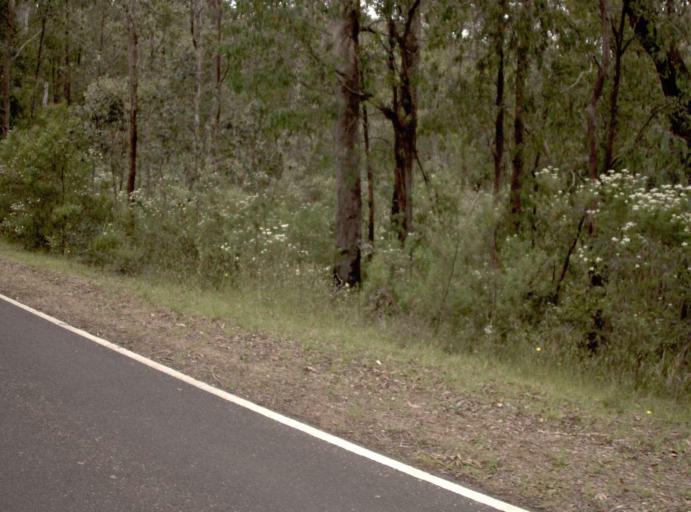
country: AU
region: Victoria
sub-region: East Gippsland
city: Bairnsdale
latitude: -37.6335
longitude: 147.2254
